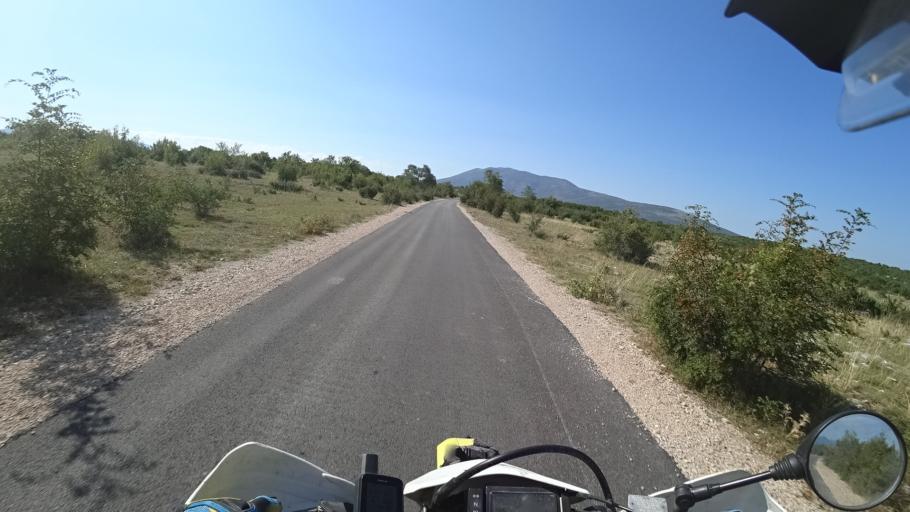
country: HR
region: Sibensko-Kniniska
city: Knin
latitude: 44.0025
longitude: 16.1942
